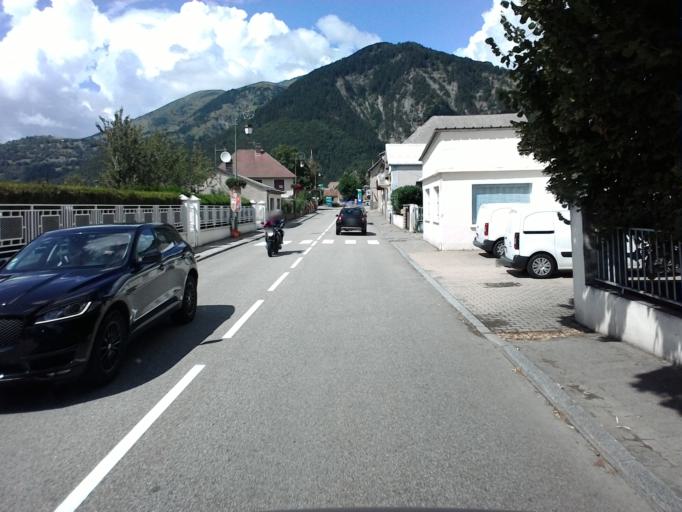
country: FR
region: Rhone-Alpes
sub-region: Departement de l'Isere
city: La Mure
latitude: 44.8156
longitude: 5.9472
